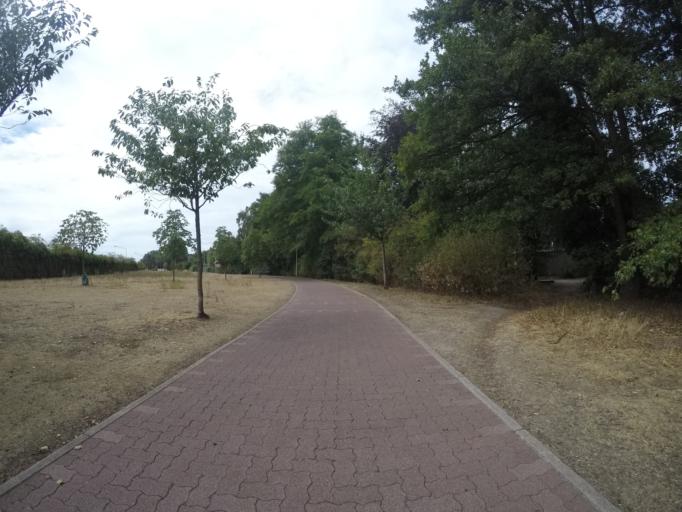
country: DE
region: North Rhine-Westphalia
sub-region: Regierungsbezirk Dusseldorf
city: Bocholt
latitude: 51.8463
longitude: 6.6000
